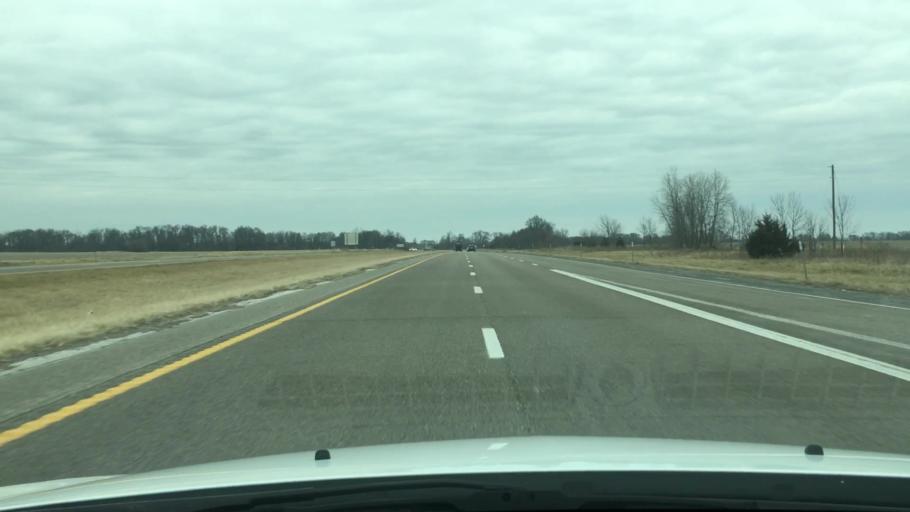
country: US
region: Missouri
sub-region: Audrain County
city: Mexico
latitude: 39.0208
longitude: -91.8858
